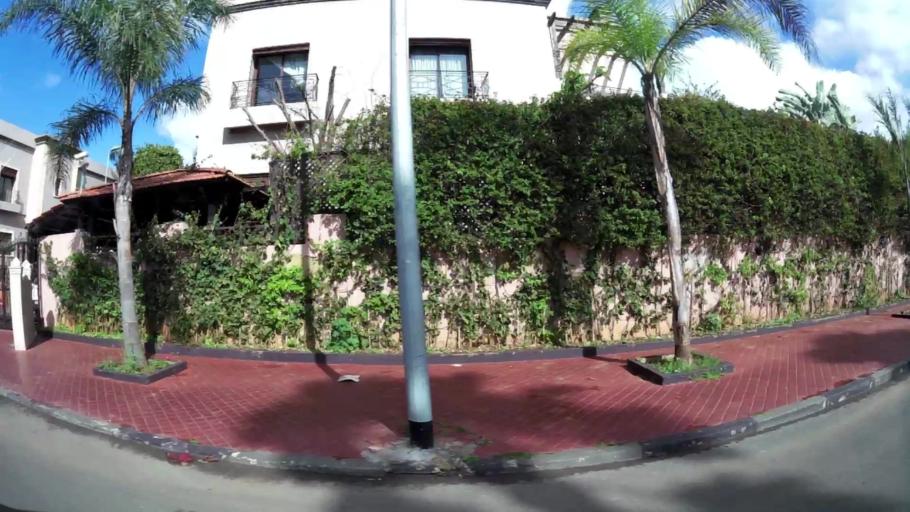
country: MA
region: Grand Casablanca
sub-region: Casablanca
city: Casablanca
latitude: 33.5439
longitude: -7.6269
